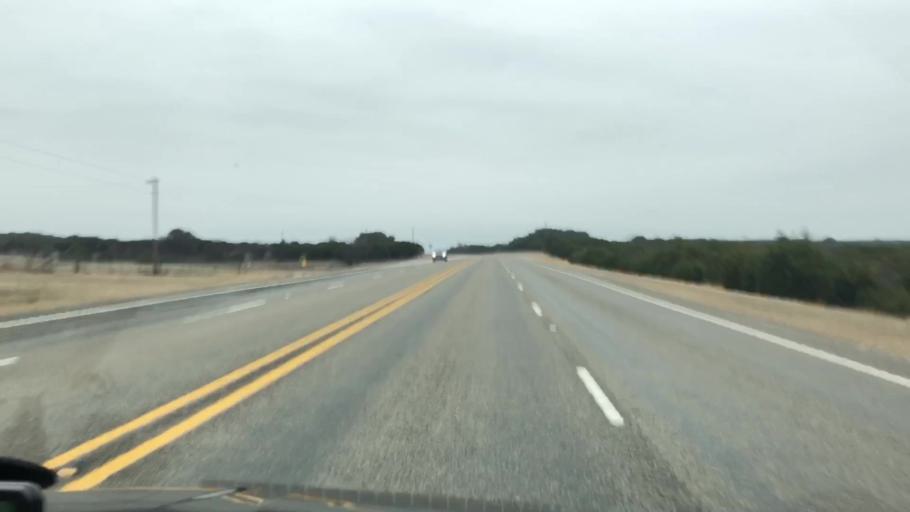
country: US
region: Texas
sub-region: Lampasas County
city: Lampasas
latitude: 31.1868
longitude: -98.1722
